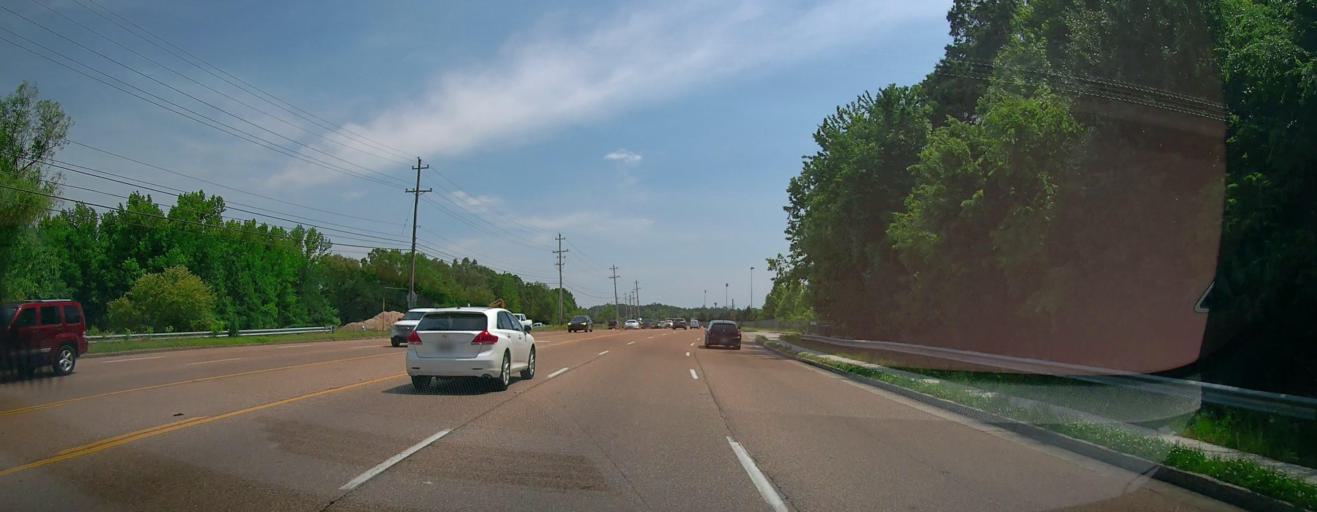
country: US
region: Tennessee
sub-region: Shelby County
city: Germantown
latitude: 35.0257
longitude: -89.7958
